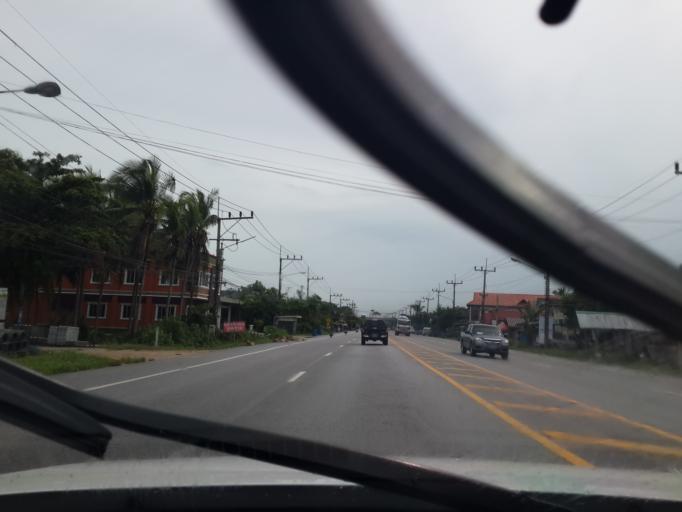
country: TH
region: Pattani
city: Nong Chik
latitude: 6.8523
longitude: 101.2050
